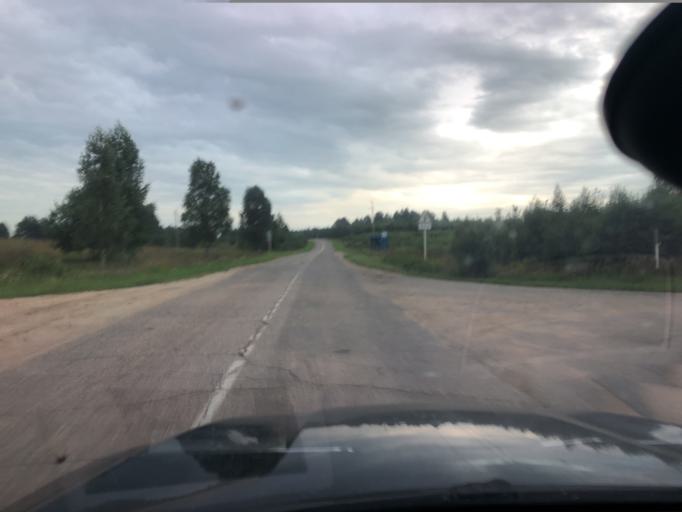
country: RU
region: Jaroslavl
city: Pereslavl'-Zalesskiy
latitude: 57.0145
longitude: 38.9597
